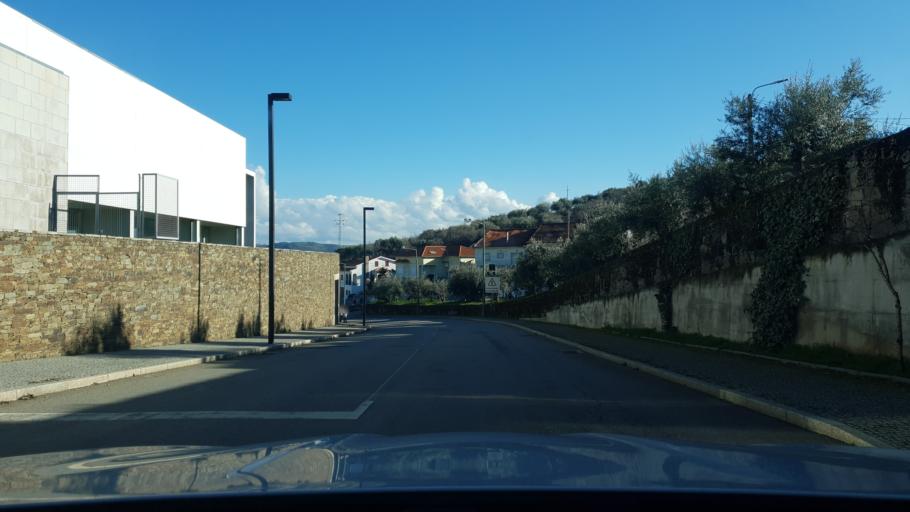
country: PT
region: Braganca
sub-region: Freixo de Espada A Cinta
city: Freixo de Espada a Cinta
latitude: 41.0946
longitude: -6.8133
